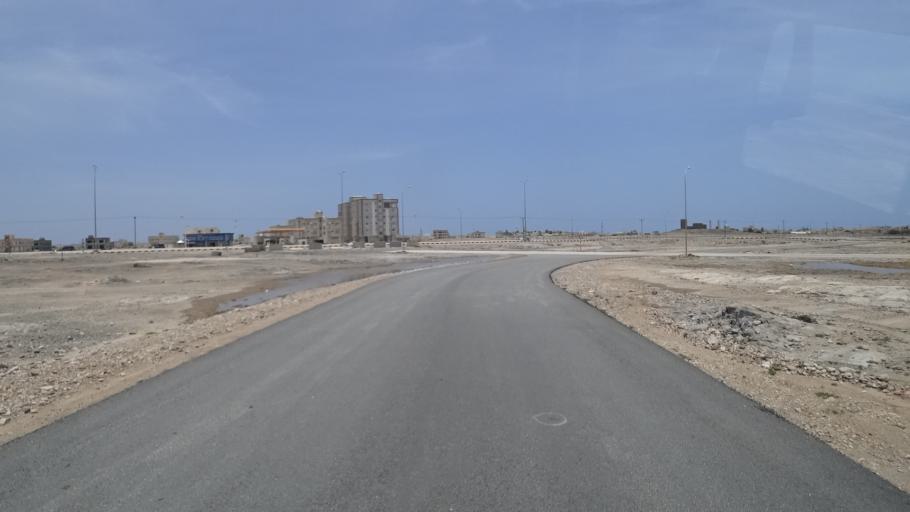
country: OM
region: Zufar
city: Salalah
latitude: 16.9976
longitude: 54.6949
